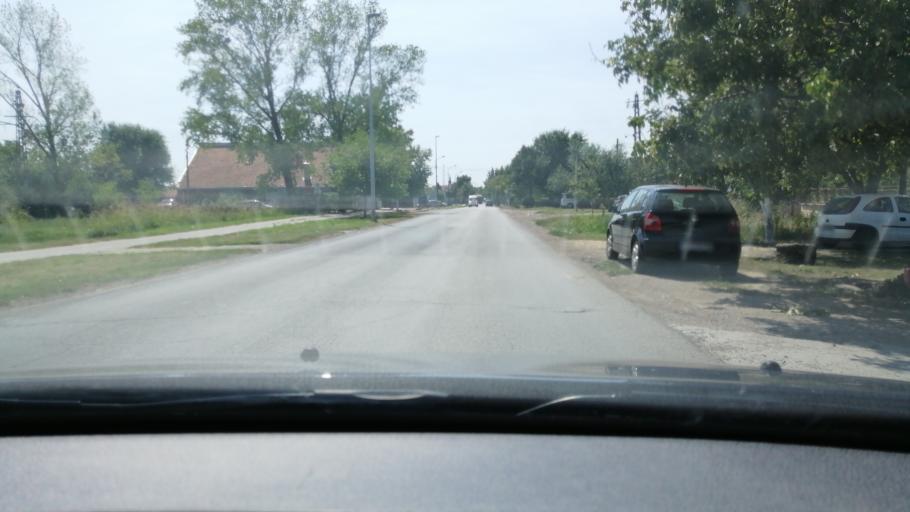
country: RS
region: Autonomna Pokrajina Vojvodina
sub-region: Srednjebanatski Okrug
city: Zrenjanin
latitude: 45.3983
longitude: 20.3931
